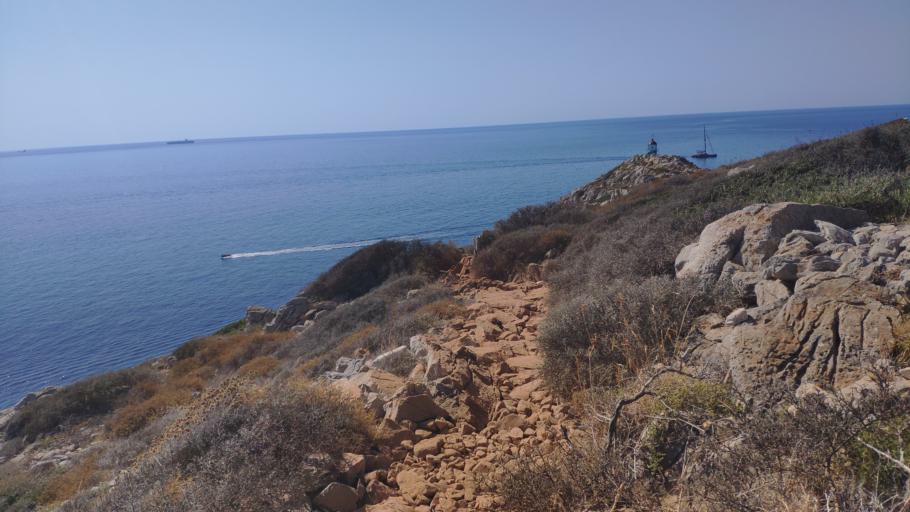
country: GR
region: Peloponnese
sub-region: Nomos Lakonias
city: Gytheio
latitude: 36.3882
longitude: 22.4827
